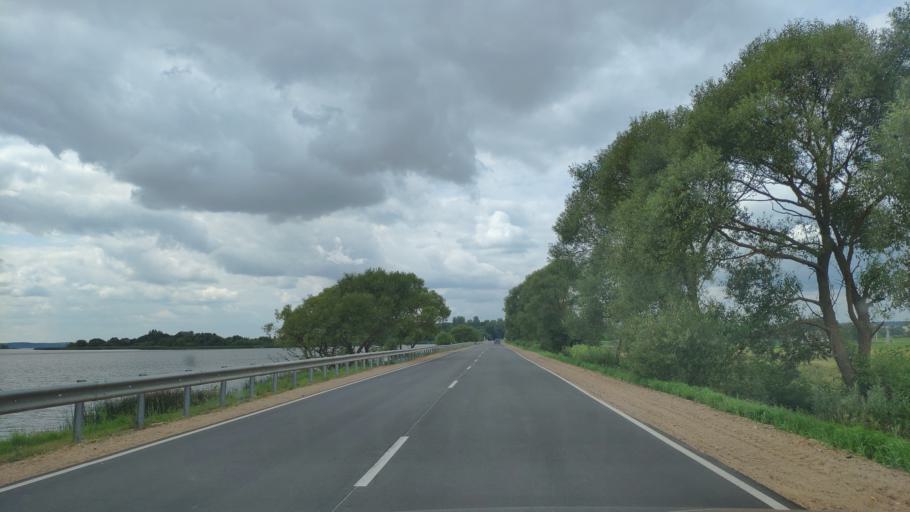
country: BY
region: Minsk
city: Syomkava
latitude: 53.9962
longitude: 27.4581
